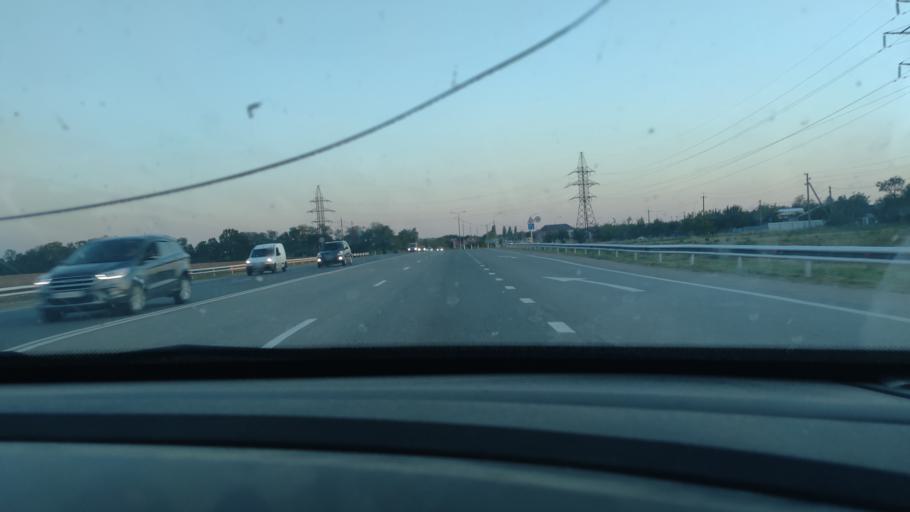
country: RU
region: Krasnodarskiy
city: Timashevsk
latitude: 45.6130
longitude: 38.9870
